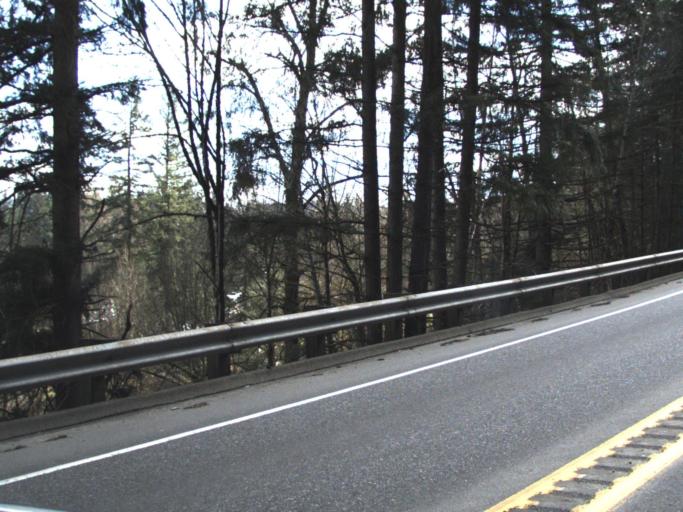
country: US
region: Washington
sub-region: King County
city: Maple Valley
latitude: 47.4009
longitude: -122.0439
